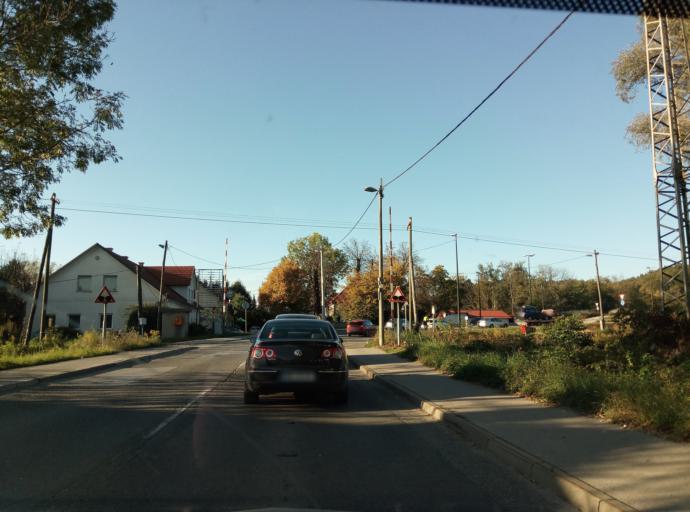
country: SI
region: Ljubljana
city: Ljubljana
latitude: 46.0985
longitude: 14.5167
